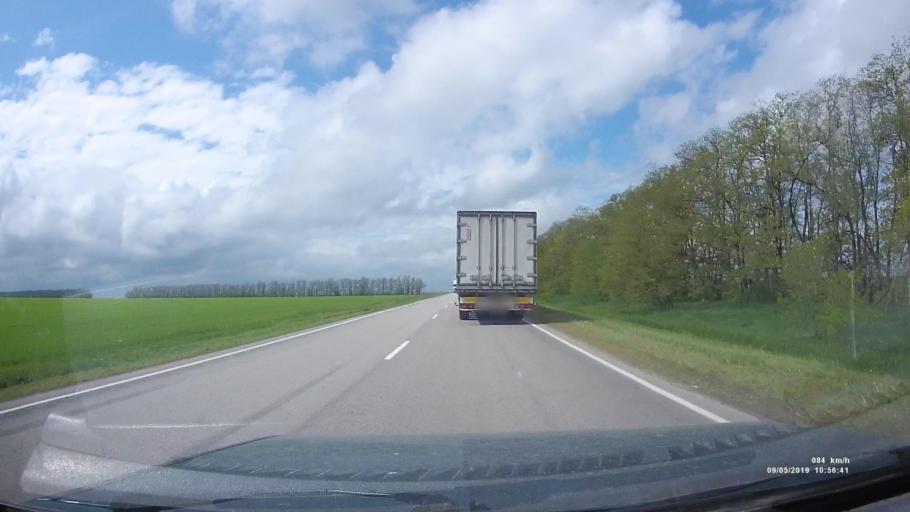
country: RU
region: Rostov
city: Peshkovo
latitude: 46.8685
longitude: 39.2934
